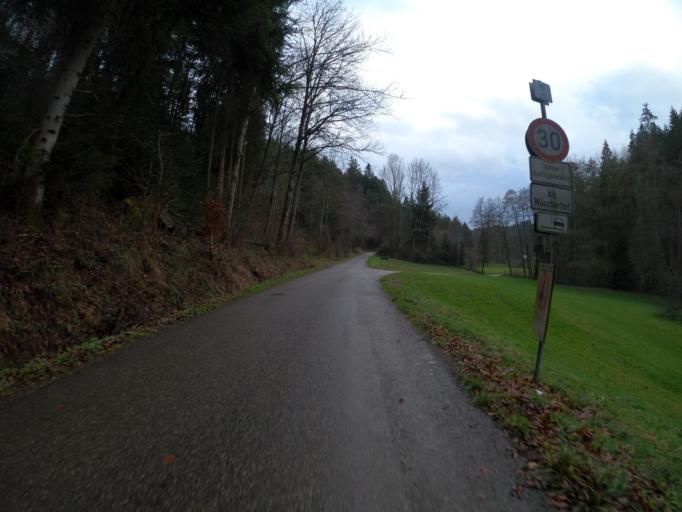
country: DE
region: Baden-Wuerttemberg
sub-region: Regierungsbezirk Stuttgart
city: Lorch
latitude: 48.7815
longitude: 9.7220
